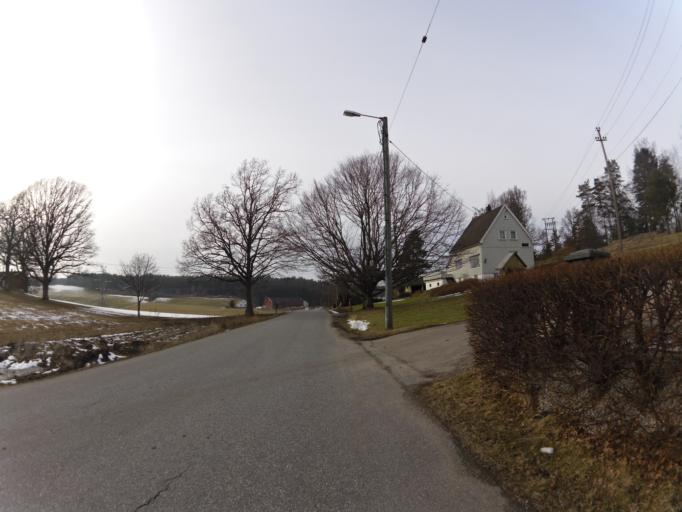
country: NO
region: Ostfold
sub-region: Fredrikstad
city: Fredrikstad
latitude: 59.2727
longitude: 11.0089
